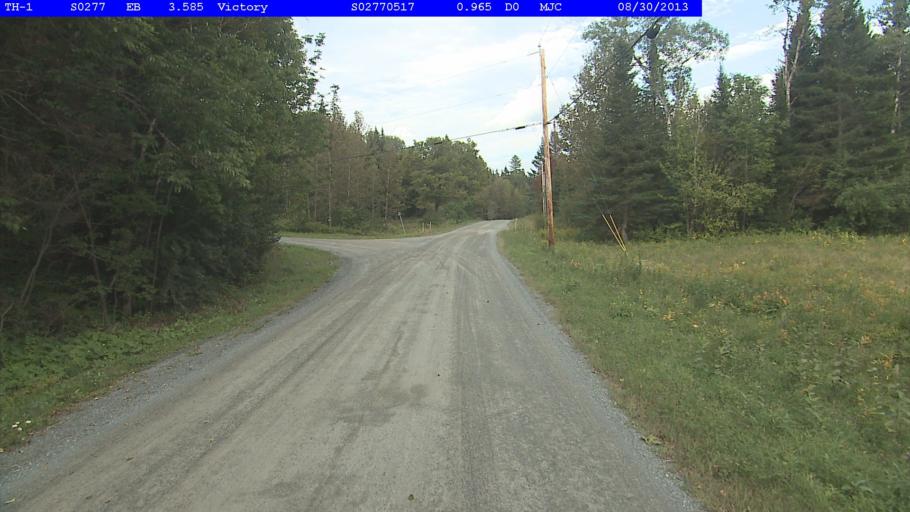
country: US
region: Vermont
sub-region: Caledonia County
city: Lyndonville
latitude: 44.5088
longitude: -71.8460
